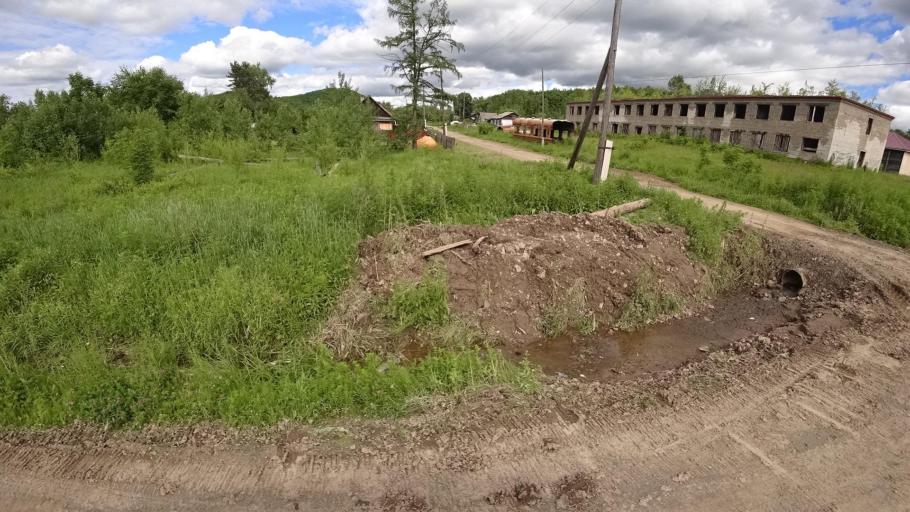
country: RU
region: Khabarovsk Krai
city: Litovko
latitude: 49.3682
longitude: 135.1735
